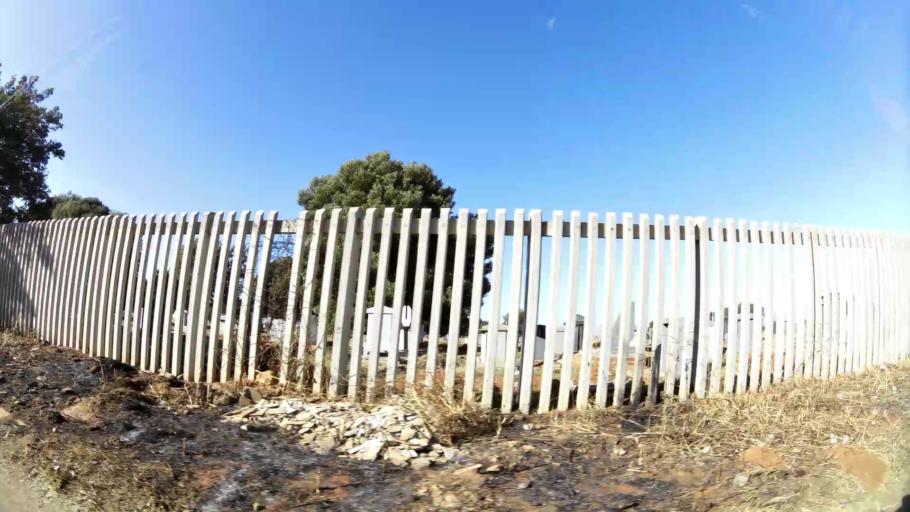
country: ZA
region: Gauteng
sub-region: Ekurhuleni Metropolitan Municipality
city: Tembisa
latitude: -26.0246
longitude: 28.2251
